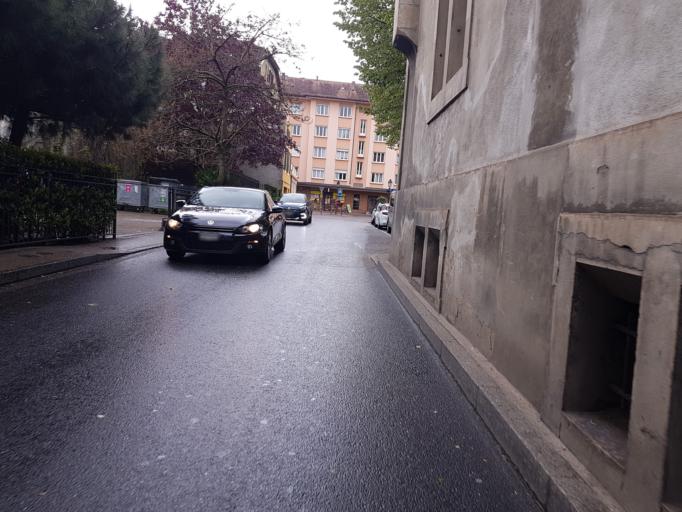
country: CH
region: Vaud
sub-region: Jura-Nord vaudois District
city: Yverdon-les-Bains
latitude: 46.7799
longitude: 6.6374
